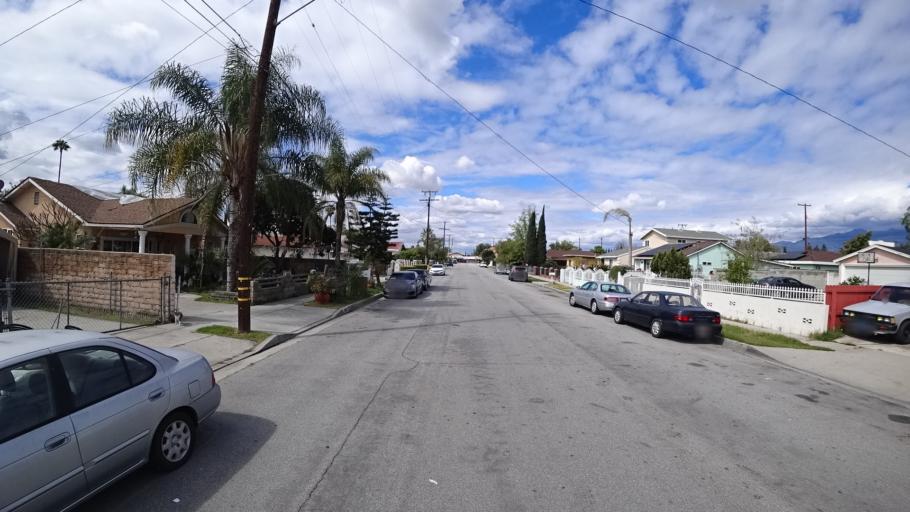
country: US
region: California
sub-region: Los Angeles County
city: Baldwin Park
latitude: 34.0940
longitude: -117.9581
